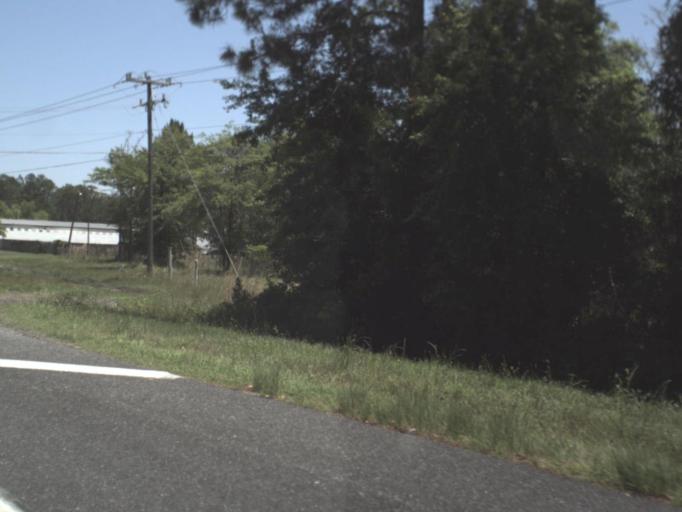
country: US
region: Florida
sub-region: Columbia County
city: Watertown
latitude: 30.1884
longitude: -82.5629
